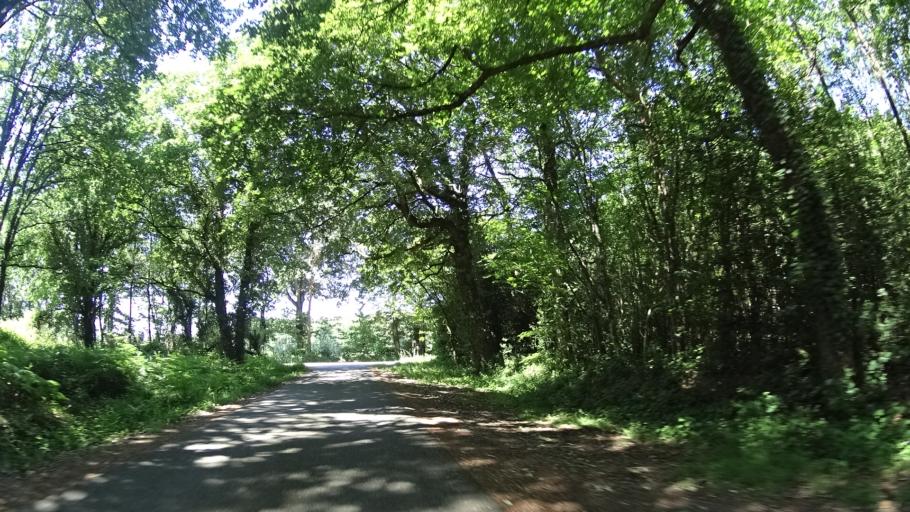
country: FR
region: Brittany
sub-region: Departement d'Ille-et-Vilaine
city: Langon
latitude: 47.7615
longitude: -1.8422
